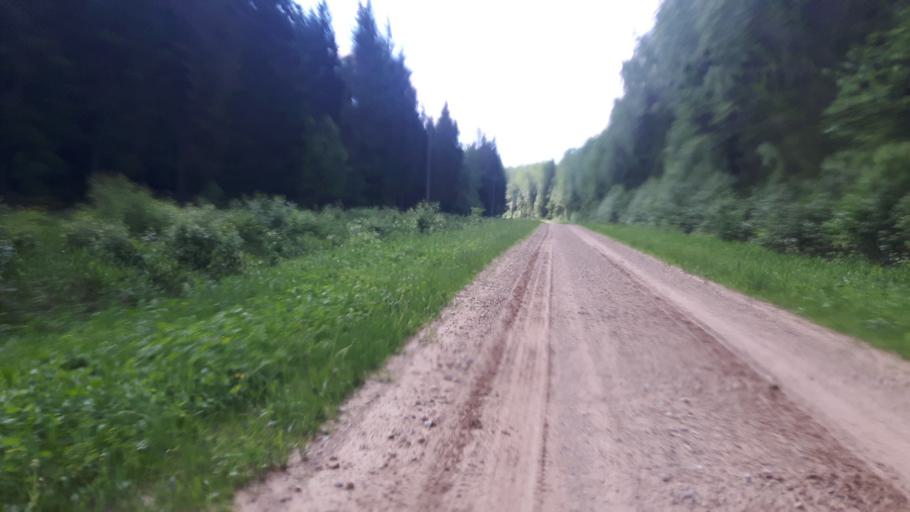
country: EE
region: Paernumaa
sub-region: Vaendra vald (alev)
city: Vandra
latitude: 58.7143
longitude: 25.0426
